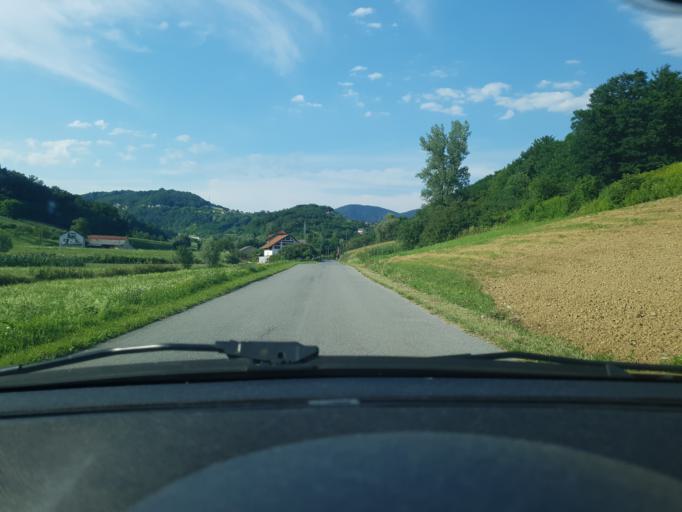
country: HR
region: Krapinsko-Zagorska
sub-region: Grad Krapina
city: Krapina
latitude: 46.1492
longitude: 15.8519
